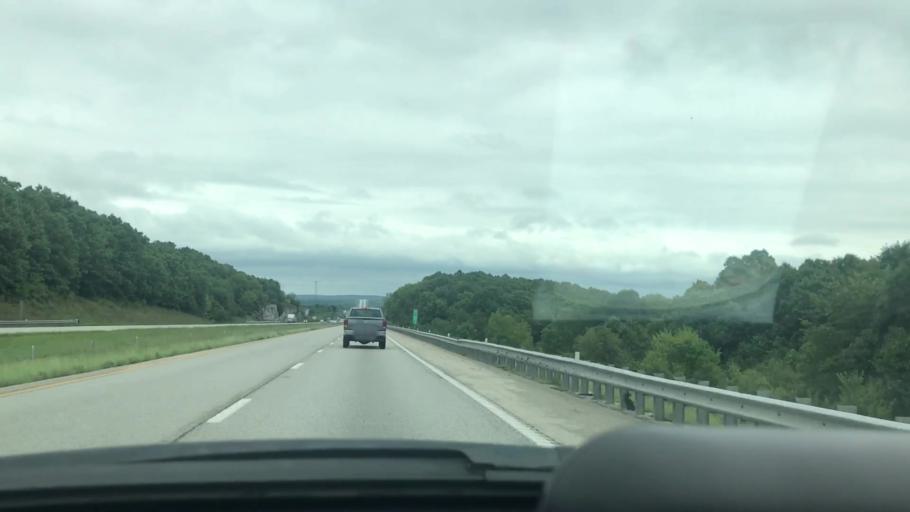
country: US
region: Missouri
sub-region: Lawrence County
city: Mount Vernon
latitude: 37.1470
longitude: -93.7090
